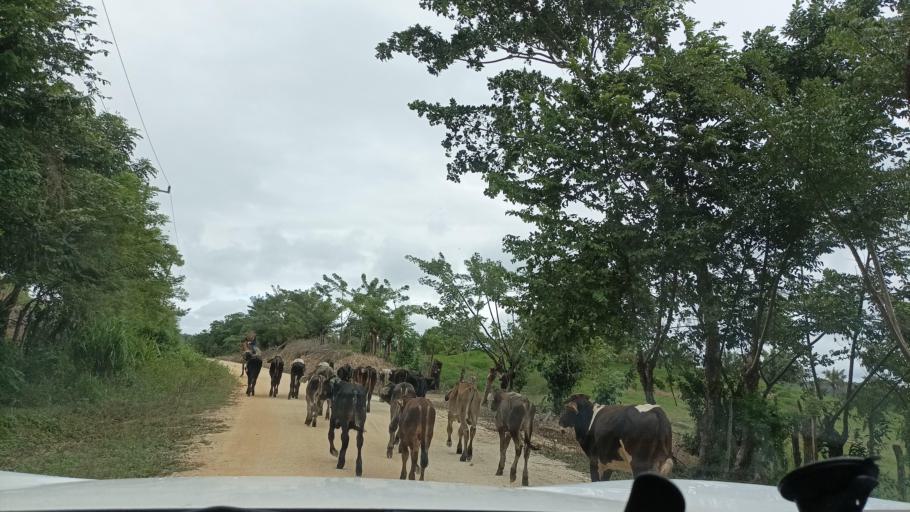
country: MX
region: Veracruz
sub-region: Moloacan
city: Cuichapa
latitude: 17.8202
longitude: -94.3536
